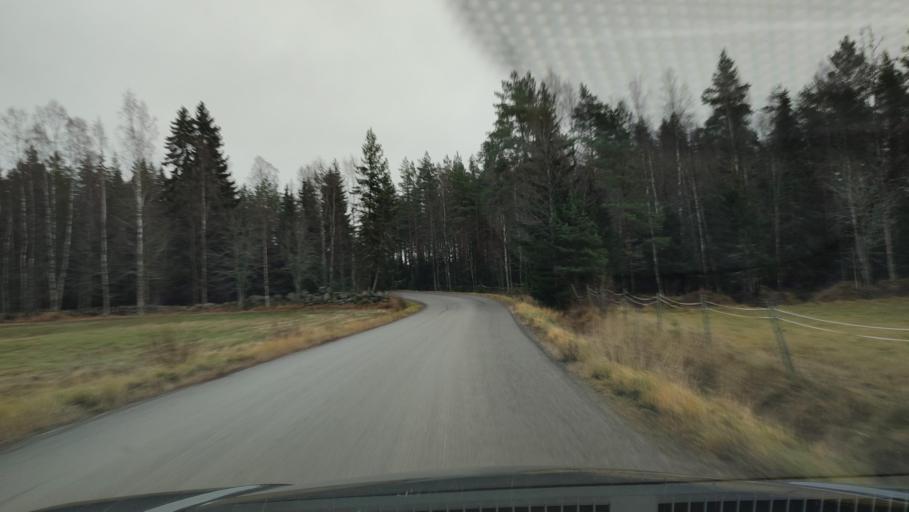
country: FI
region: Southern Ostrobothnia
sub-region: Suupohja
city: Karijoki
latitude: 62.1266
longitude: 21.5928
